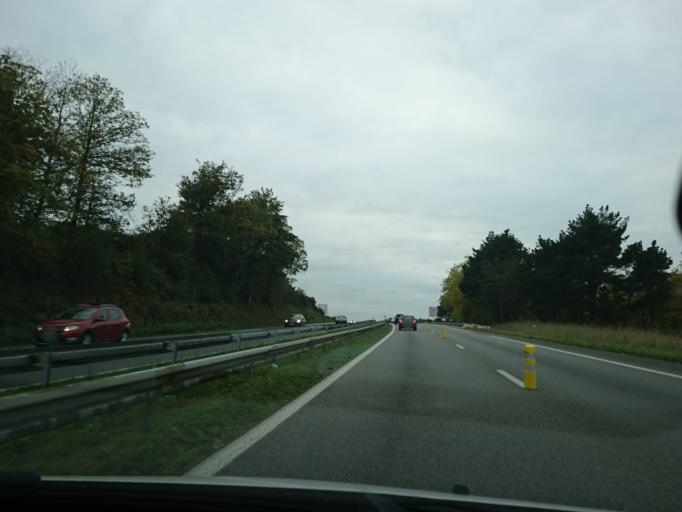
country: FR
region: Brittany
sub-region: Departement du Morbihan
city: Muzillac
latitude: 47.5490
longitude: -2.4500
